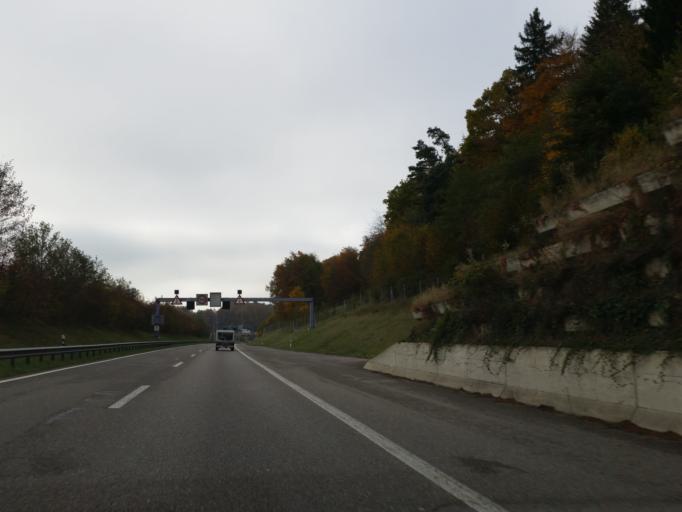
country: CH
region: Fribourg
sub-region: Broye District
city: Estavayer-le-Lac
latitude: 46.8195
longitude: 6.8204
